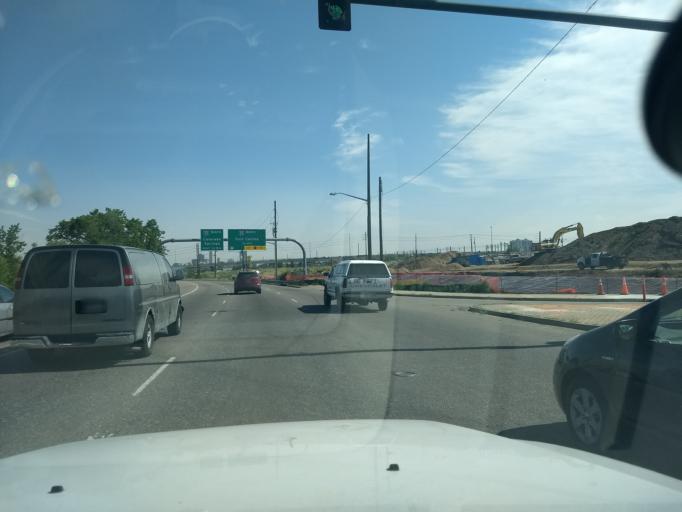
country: US
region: Colorado
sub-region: Denver County
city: Denver
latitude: 39.6968
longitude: -104.9918
